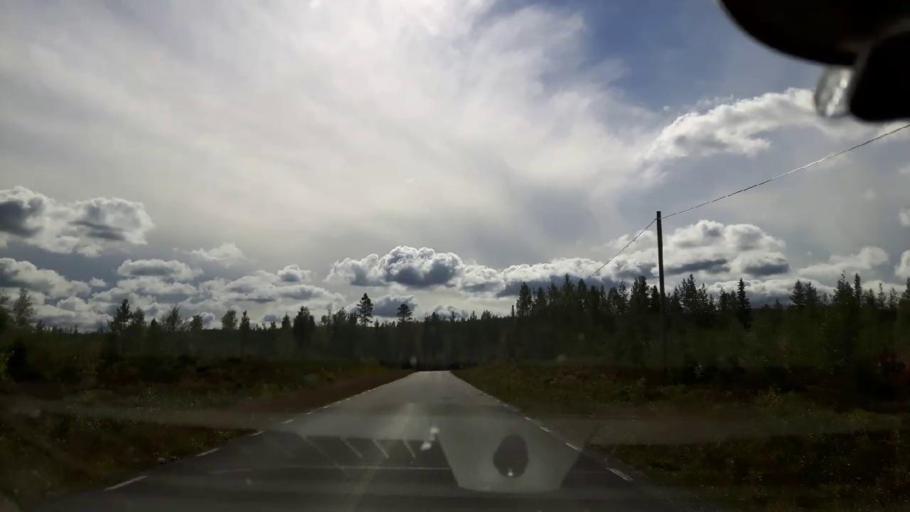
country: SE
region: Jaemtland
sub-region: Braecke Kommun
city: Braecke
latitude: 63.1950
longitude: 15.3688
